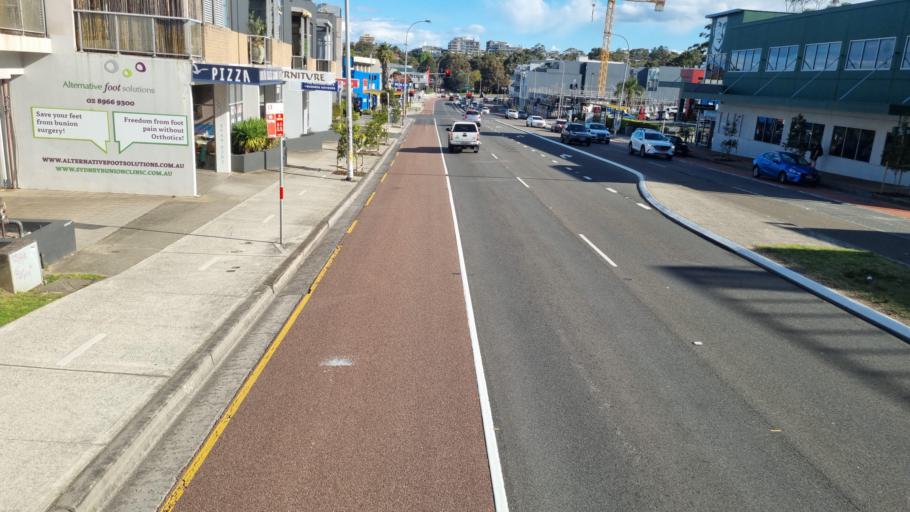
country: AU
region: New South Wales
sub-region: Warringah
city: North Manly
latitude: -33.7854
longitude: 151.2670
